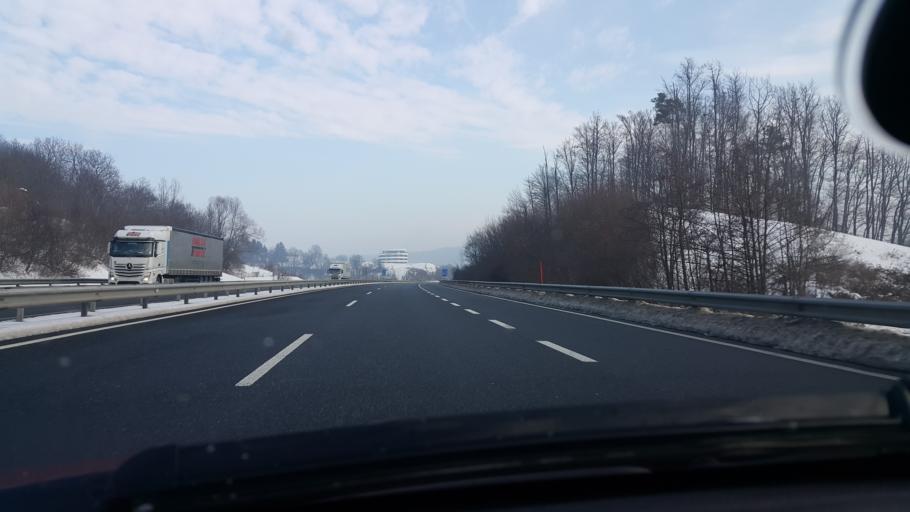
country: SI
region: Sentilj
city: Sentilj v Slov. Goricah
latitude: 46.6704
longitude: 15.6452
